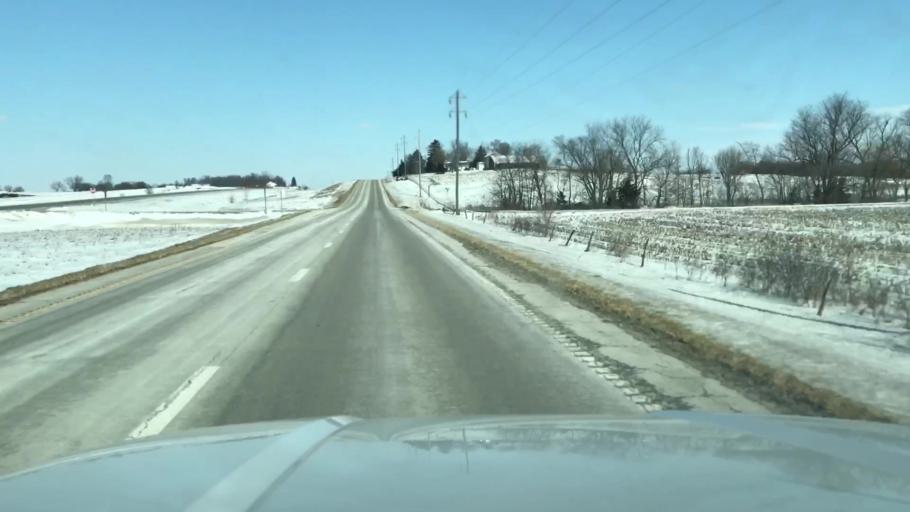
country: US
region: Missouri
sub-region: Nodaway County
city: Maryville
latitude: 40.1486
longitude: -94.8691
